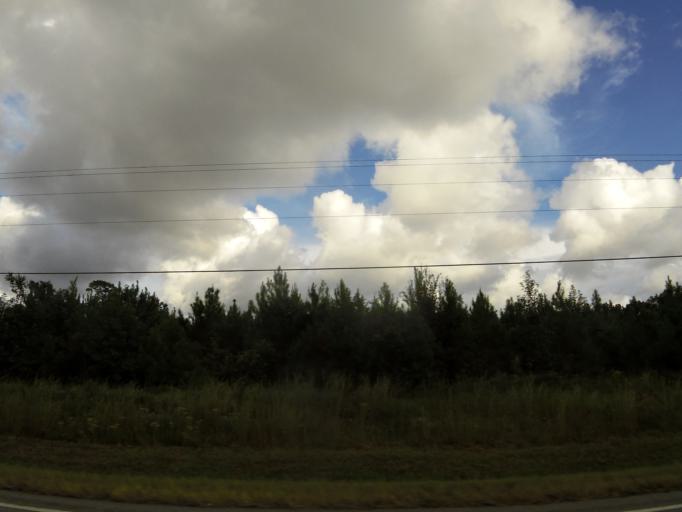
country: US
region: Georgia
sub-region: Liberty County
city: Midway
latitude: 31.7777
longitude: -81.4422
